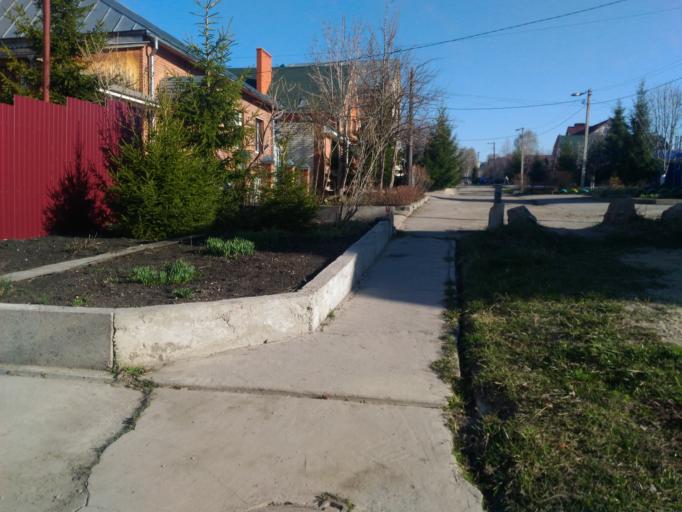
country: RU
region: Ulyanovsk
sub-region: Ulyanovskiy Rayon
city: Ulyanovsk
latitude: 54.3388
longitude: 48.3878
